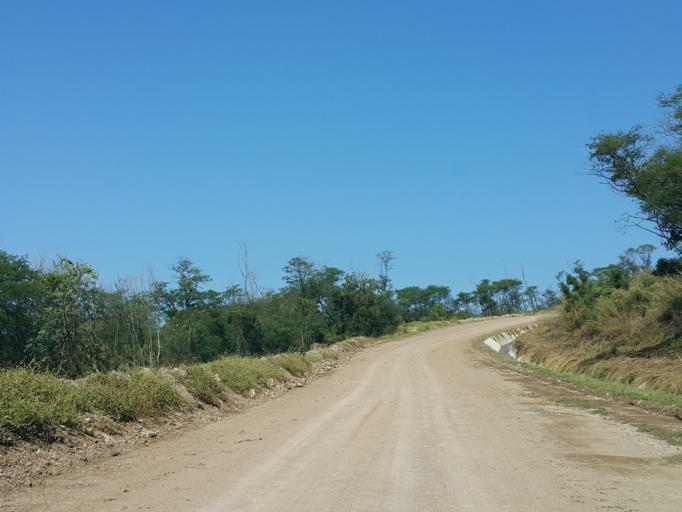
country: TH
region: Lampang
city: Mae Mo
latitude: 18.3253
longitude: 99.7375
